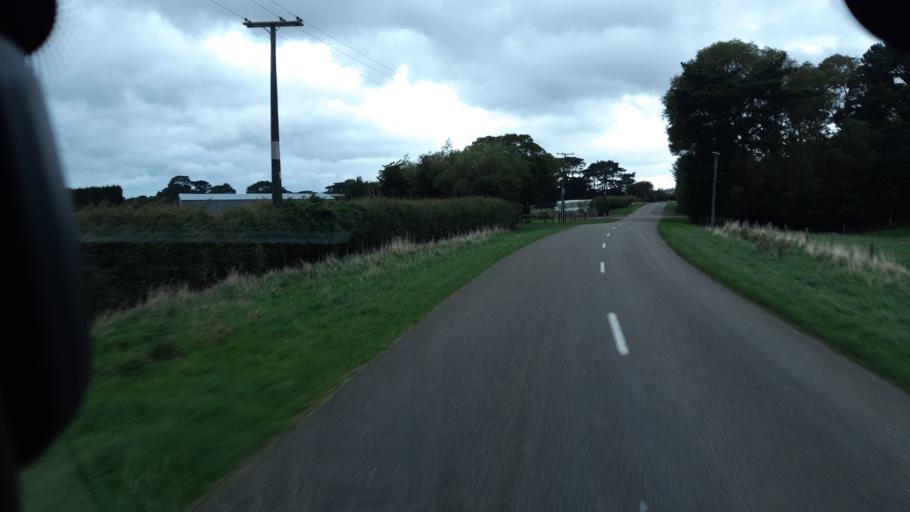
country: NZ
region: Manawatu-Wanganui
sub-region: Palmerston North City
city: Palmerston North
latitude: -40.6112
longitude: 175.6421
